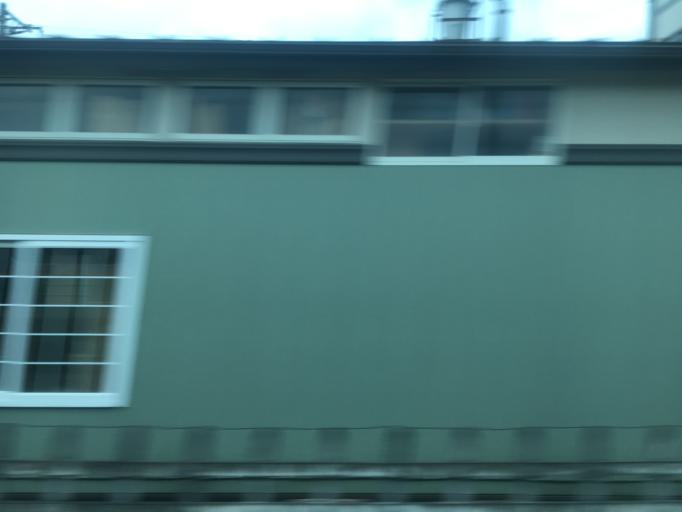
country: JP
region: Saitama
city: Ageoshimo
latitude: 35.9602
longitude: 139.5985
